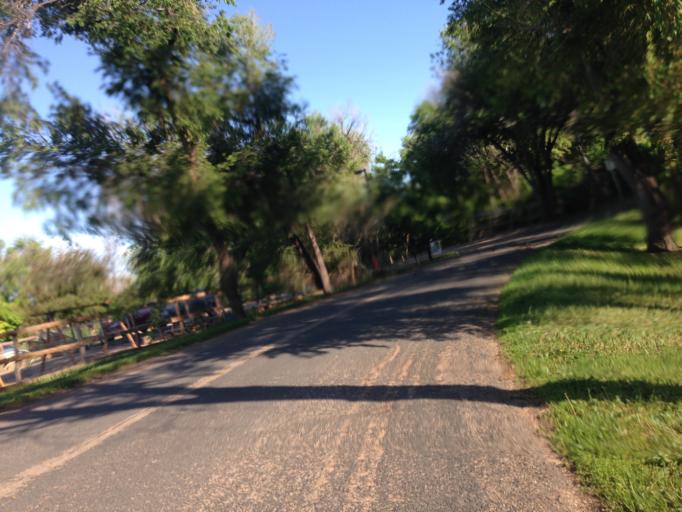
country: US
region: Colorado
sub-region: Boulder County
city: Lafayette
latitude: 40.0163
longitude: -105.1047
